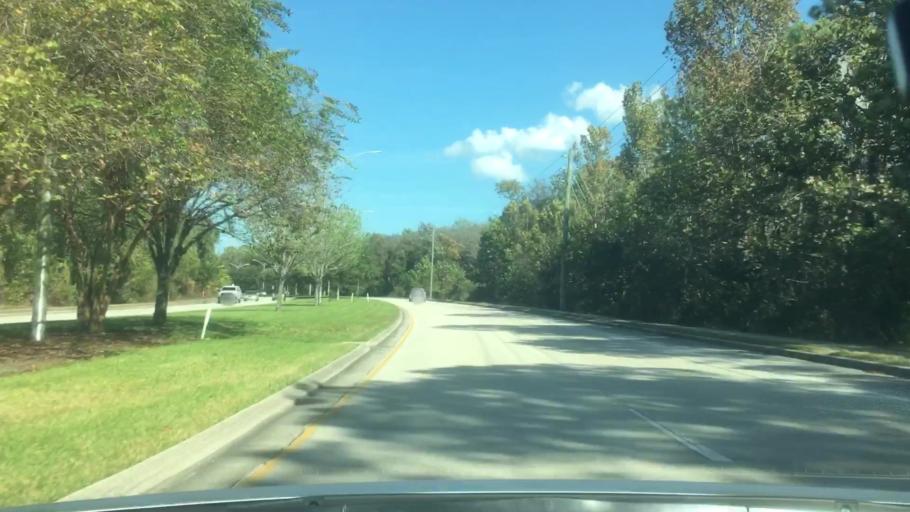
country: US
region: Florida
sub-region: Duval County
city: Atlantic Beach
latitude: 30.3539
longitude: -81.5074
